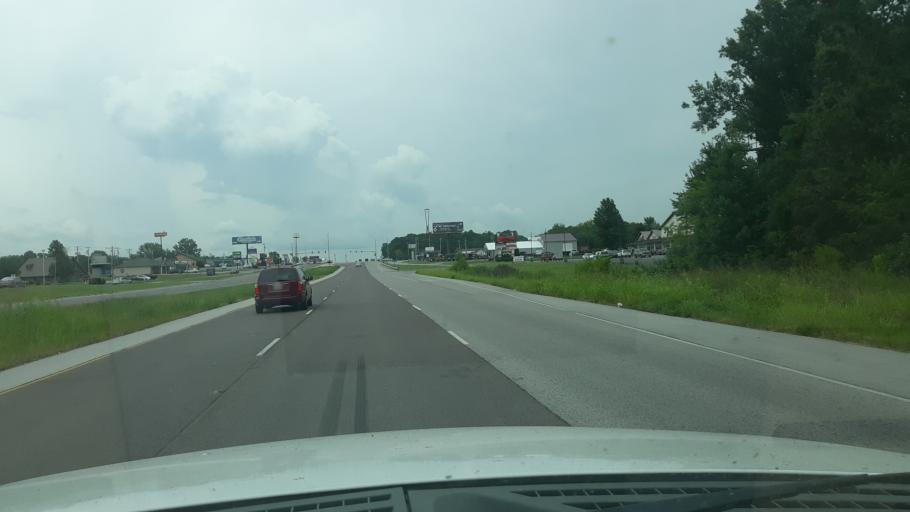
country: US
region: Illinois
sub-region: Williamson County
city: Carterville
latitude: 37.7450
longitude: -89.0828
